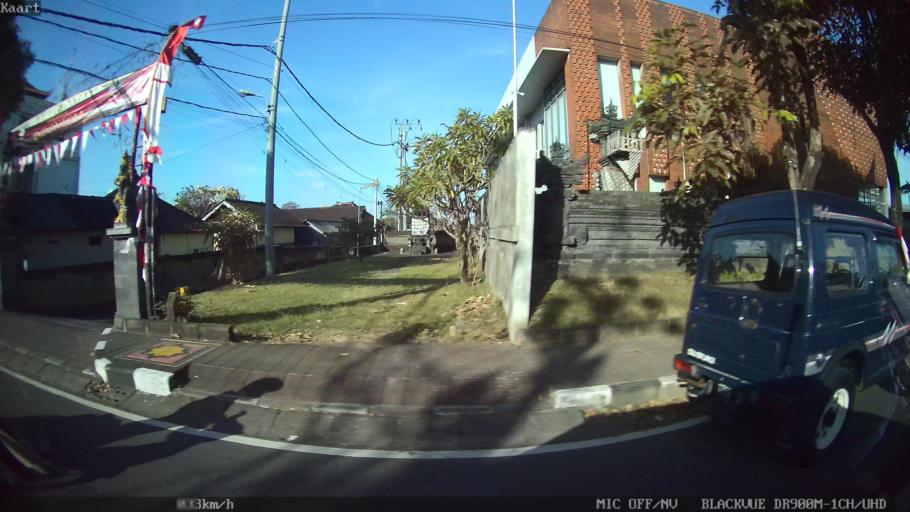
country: ID
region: Bali
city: Banjar Karangsuling
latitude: -8.6113
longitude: 115.1919
